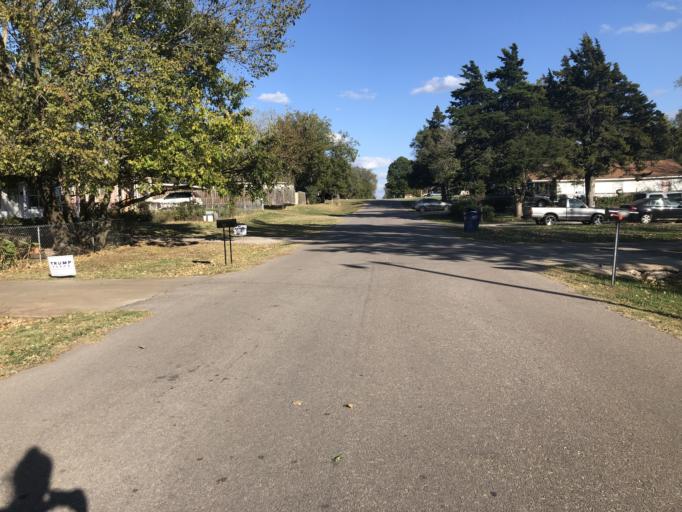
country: US
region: Oklahoma
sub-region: Pottawatomie County
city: Tecumseh
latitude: 35.2555
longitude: -96.9406
